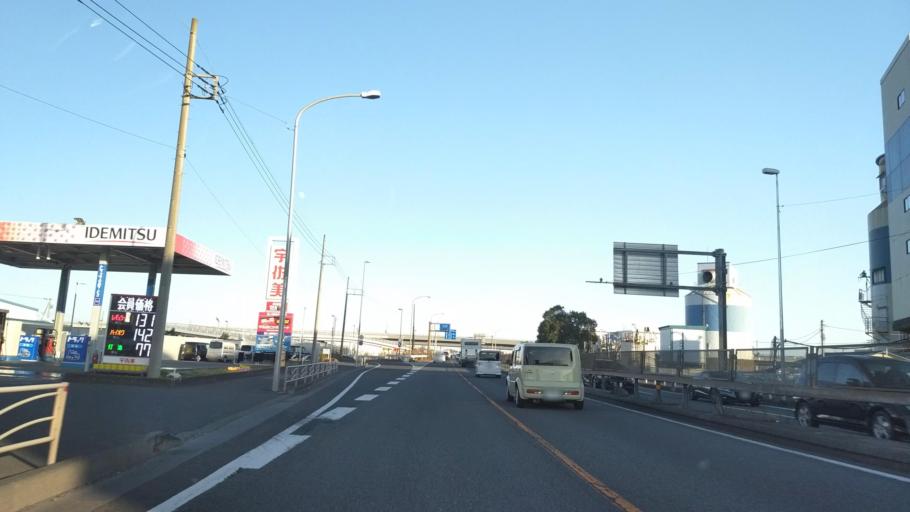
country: JP
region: Kanagawa
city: Zama
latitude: 35.4650
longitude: 139.3738
